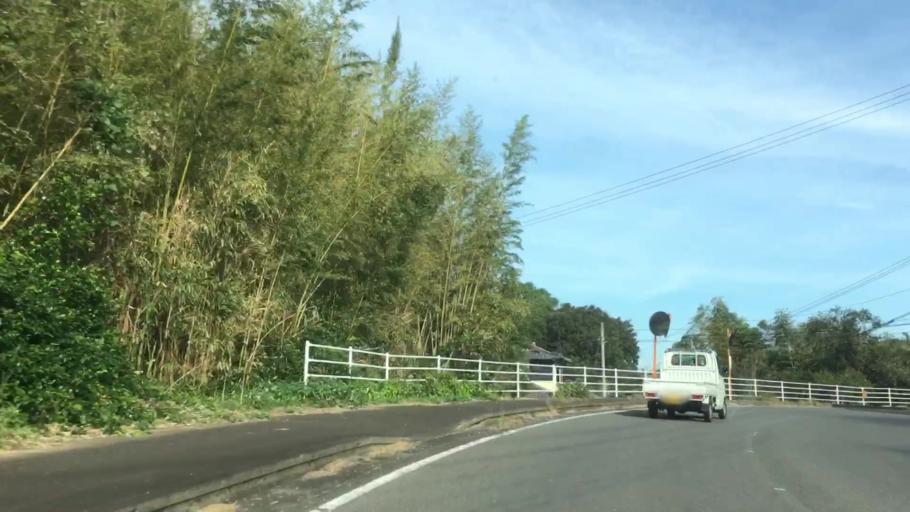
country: JP
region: Nagasaki
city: Sasebo
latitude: 33.0122
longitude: 129.6541
